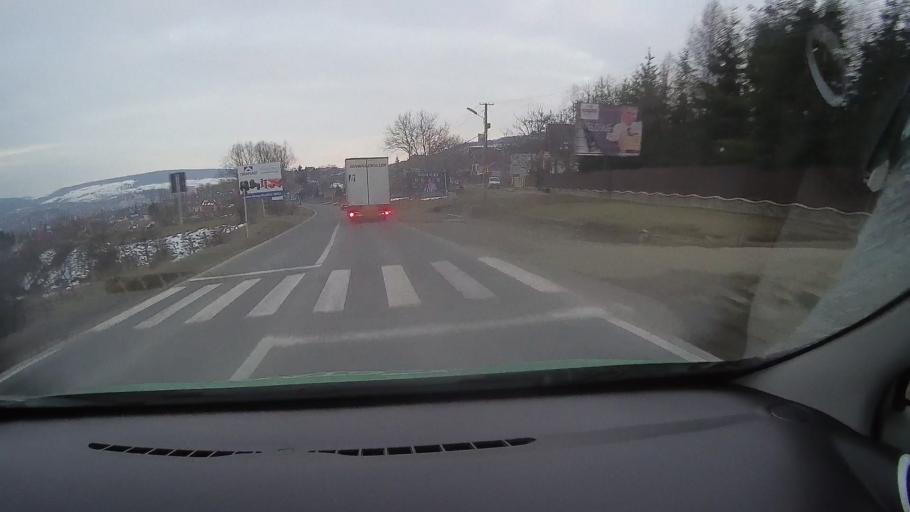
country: RO
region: Harghita
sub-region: Municipiul Odorheiu Secuiesc
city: Odorheiu Secuiesc
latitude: 46.3198
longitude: 25.2800
